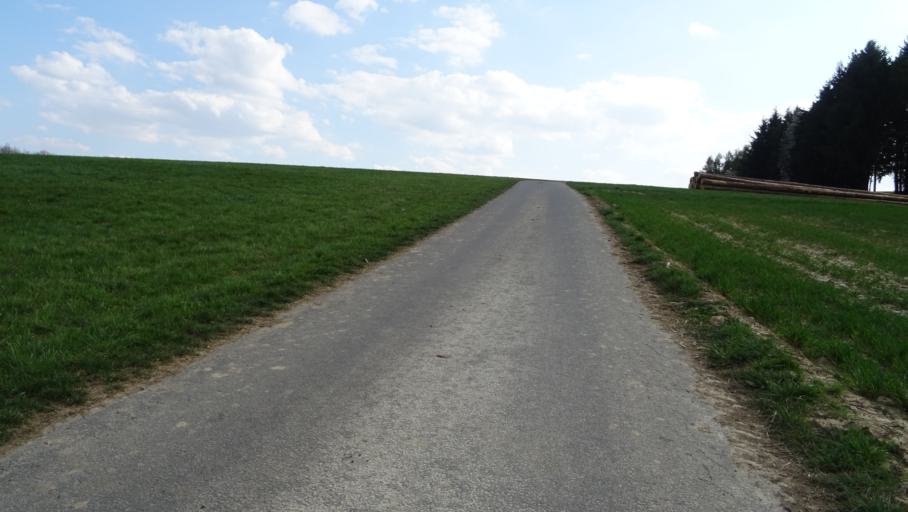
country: DE
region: Baden-Wuerttemberg
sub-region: Karlsruhe Region
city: Billigheim
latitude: 49.3830
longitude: 9.2436
